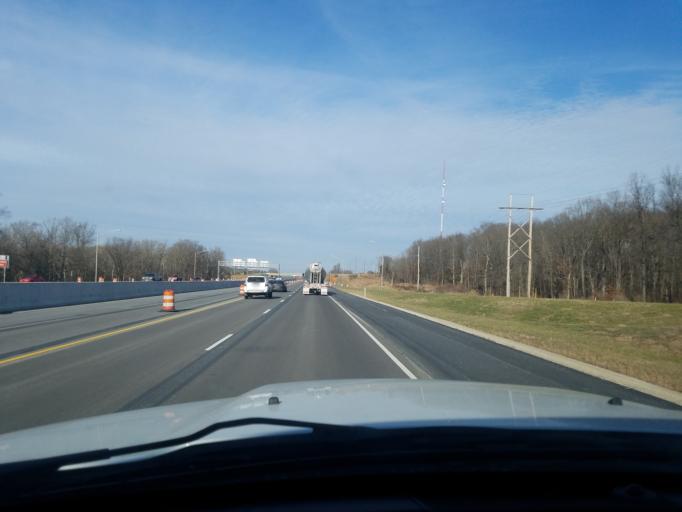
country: US
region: Indiana
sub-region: Monroe County
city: Bloomington
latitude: 39.1894
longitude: -86.5546
